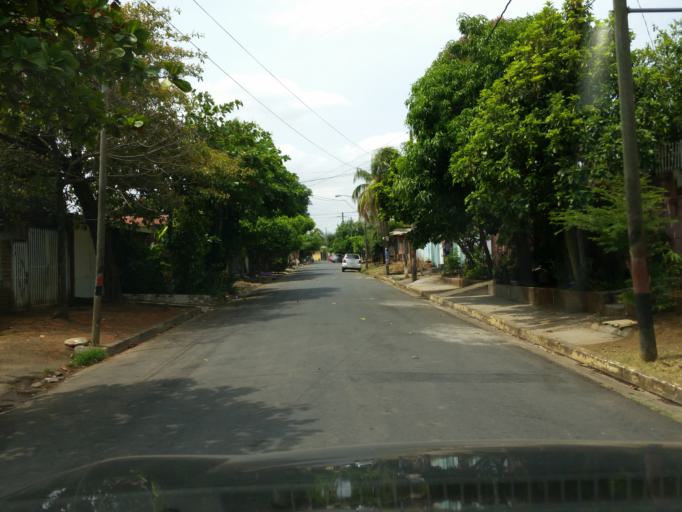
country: NI
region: Managua
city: Managua
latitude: 12.1196
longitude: -86.2716
